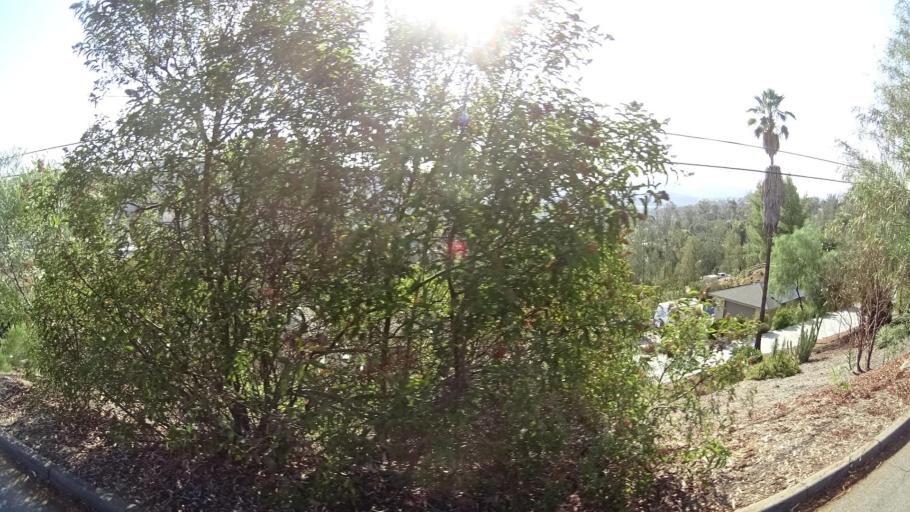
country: US
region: California
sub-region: San Diego County
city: Eucalyptus Hills
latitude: 32.8894
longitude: -116.9391
